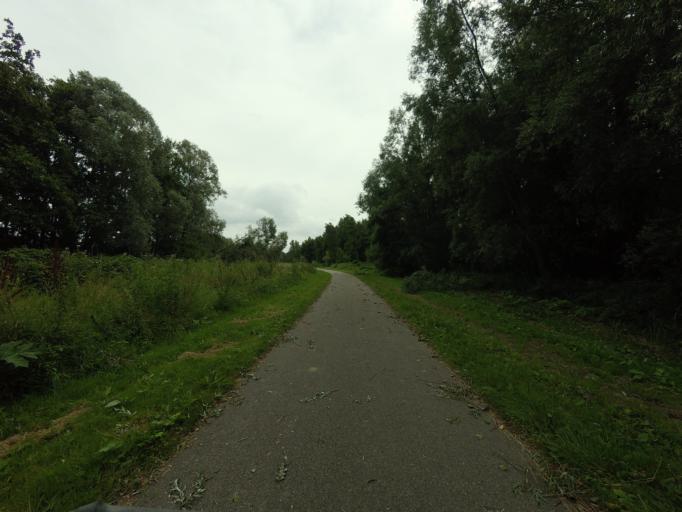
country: NL
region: North Holland
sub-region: Gemeente Amsterdam
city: Driemond
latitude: 52.3227
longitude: 5.0084
